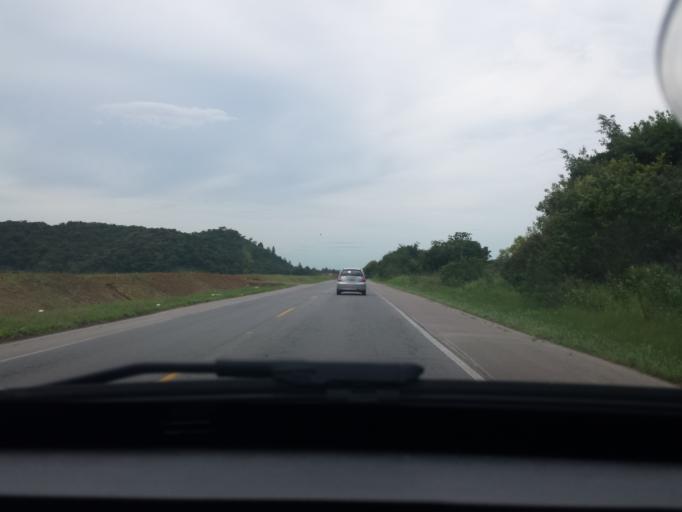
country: BR
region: Santa Catarina
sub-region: Gaspar
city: Gaspar
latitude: -26.8817
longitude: -48.8559
